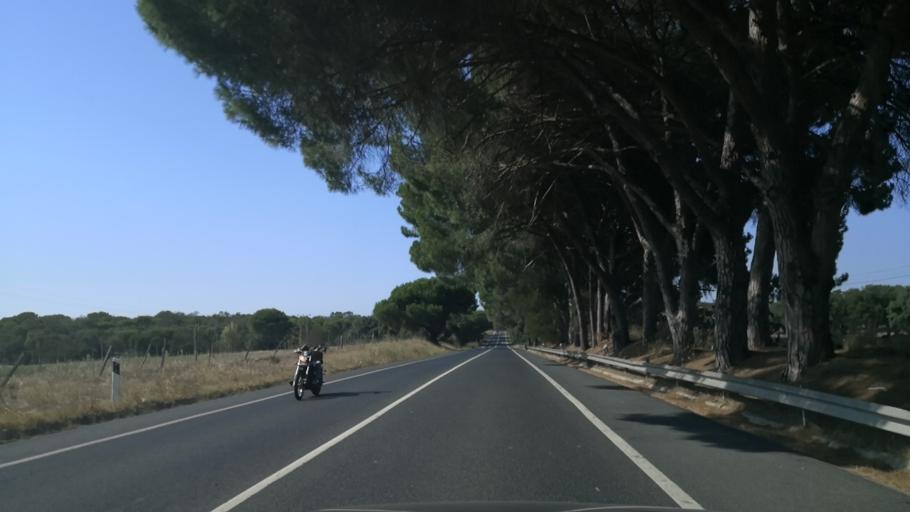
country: PT
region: Evora
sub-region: Vendas Novas
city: Vendas Novas
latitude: 38.7038
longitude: -8.6127
